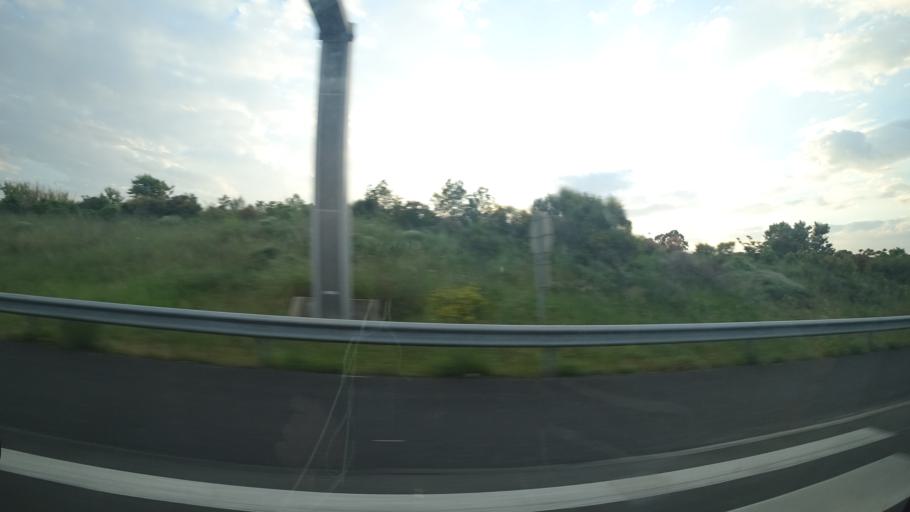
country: FR
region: Languedoc-Roussillon
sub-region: Departement de l'Herault
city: Lezignan-la-Cebe
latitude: 43.4799
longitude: 3.4374
